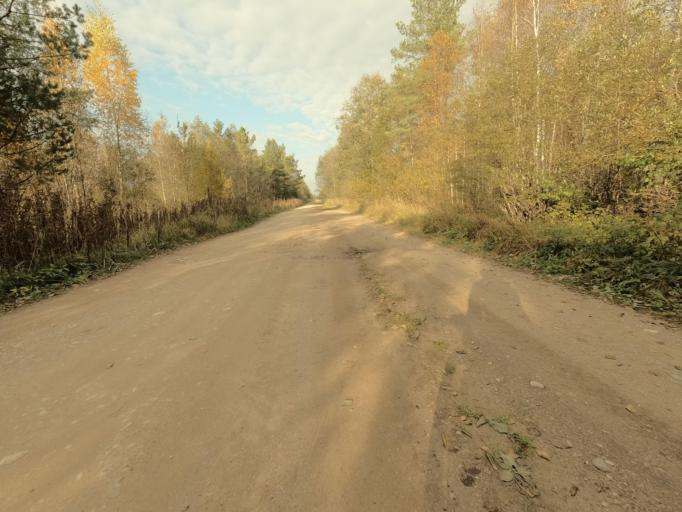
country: RU
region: Novgorod
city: Volkhovskiy
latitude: 58.8982
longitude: 31.0315
